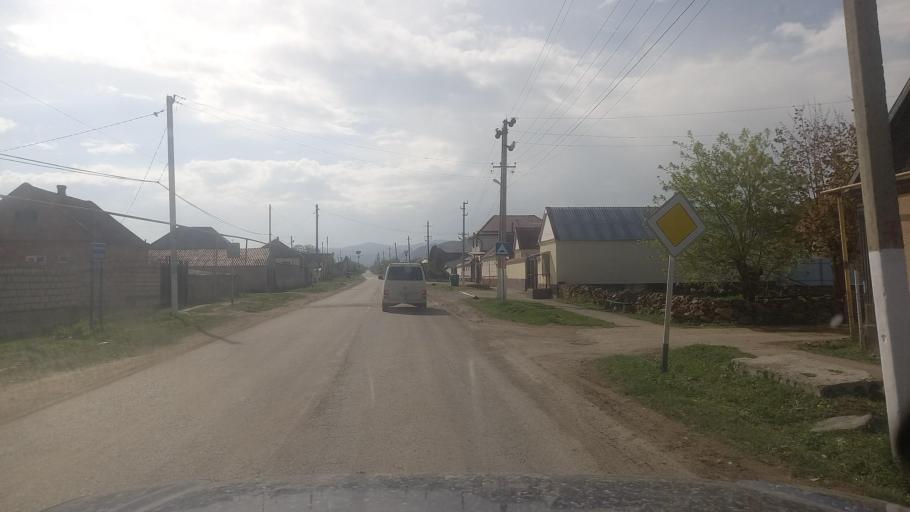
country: RU
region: Kabardino-Balkariya
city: Kamennomostskoye
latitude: 43.7348
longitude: 43.0408
